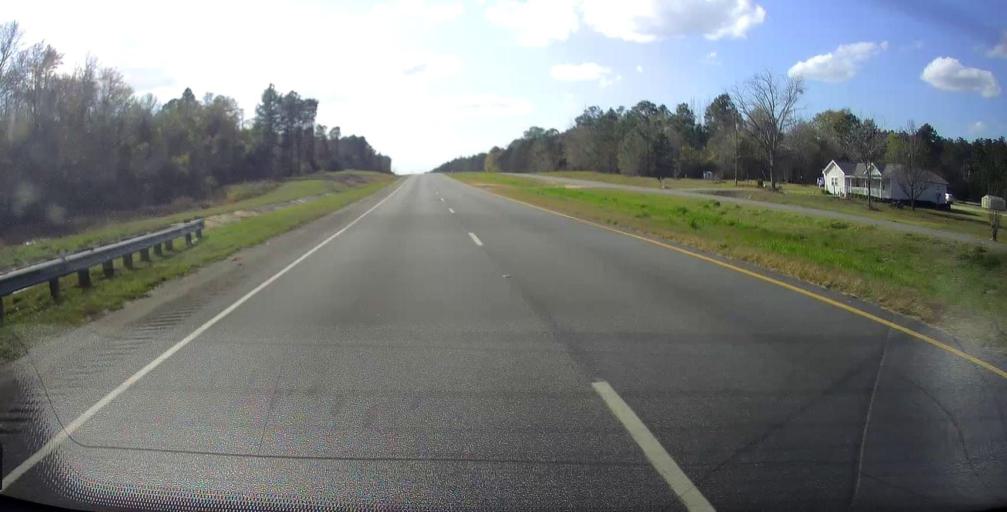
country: US
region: Georgia
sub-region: Telfair County
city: Helena
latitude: 32.1027
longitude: -83.0164
